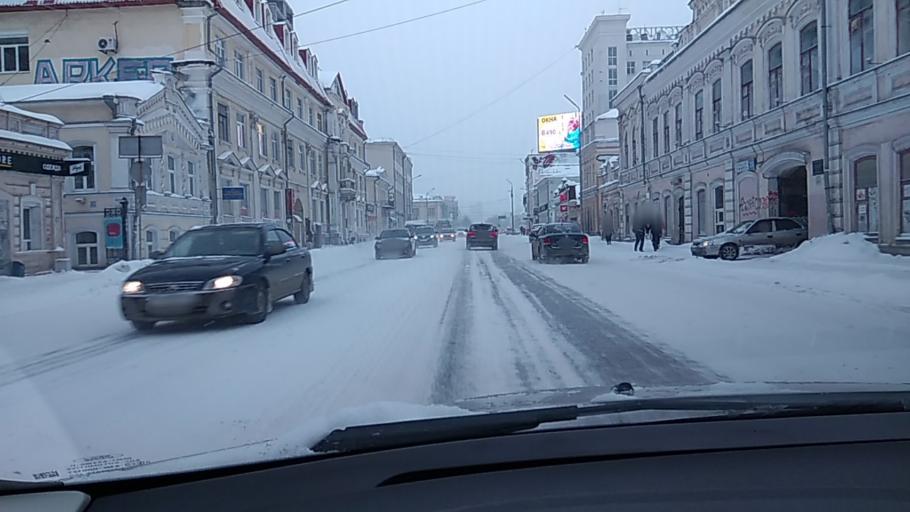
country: RU
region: Sverdlovsk
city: Yekaterinburg
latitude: 56.8323
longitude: 60.6005
